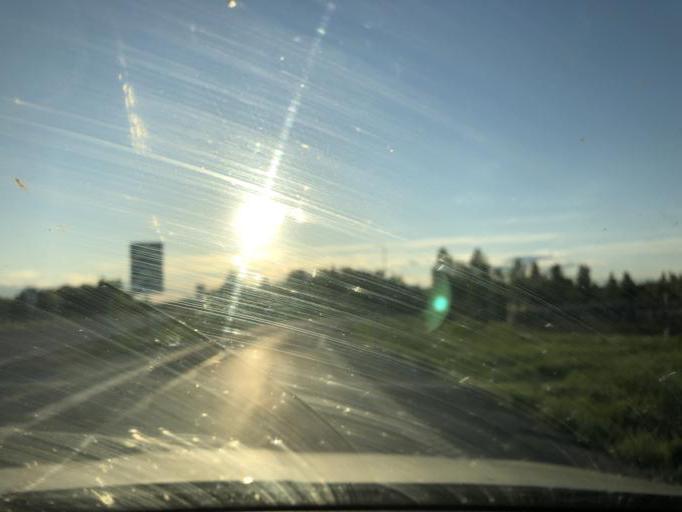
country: SE
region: Norrbotten
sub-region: Lulea Kommun
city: Sodra Sunderbyn
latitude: 65.6658
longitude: 21.9435
